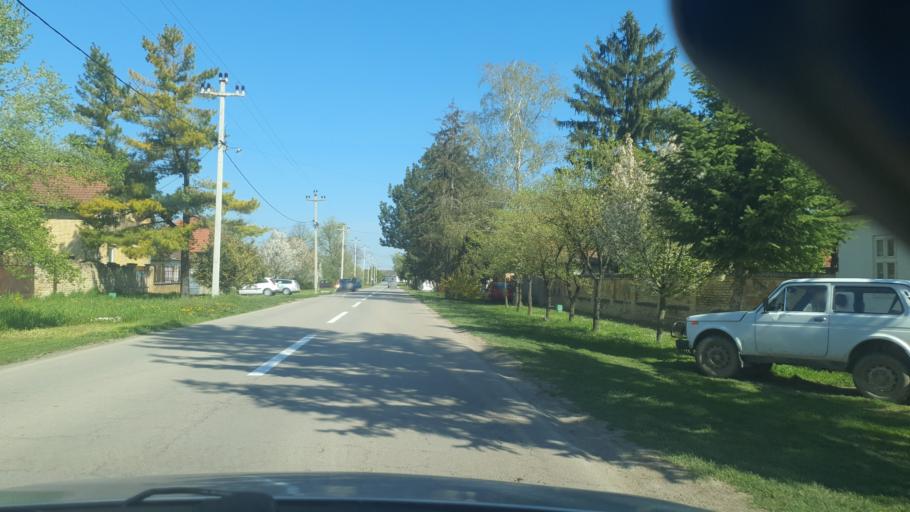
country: RS
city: Kolut
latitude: 45.8555
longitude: 18.9322
